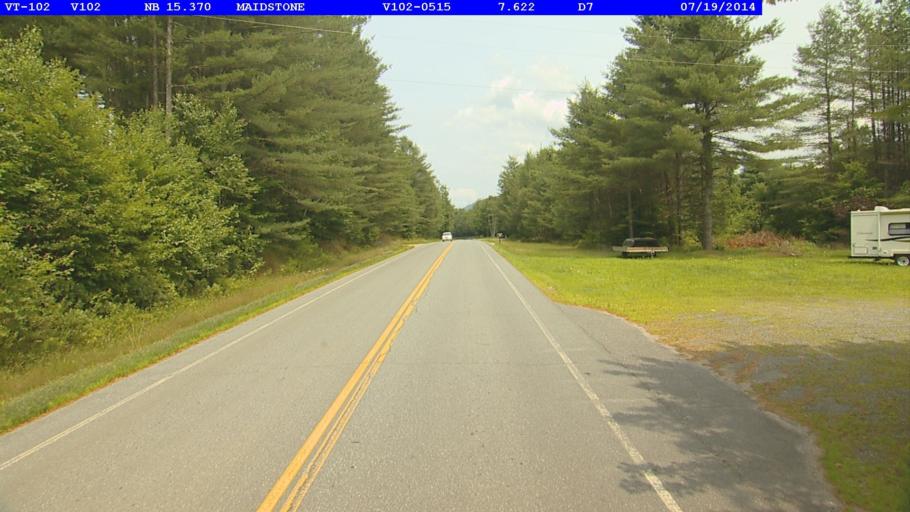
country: US
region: New Hampshire
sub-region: Coos County
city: Stratford
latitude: 44.6597
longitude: -71.5911
